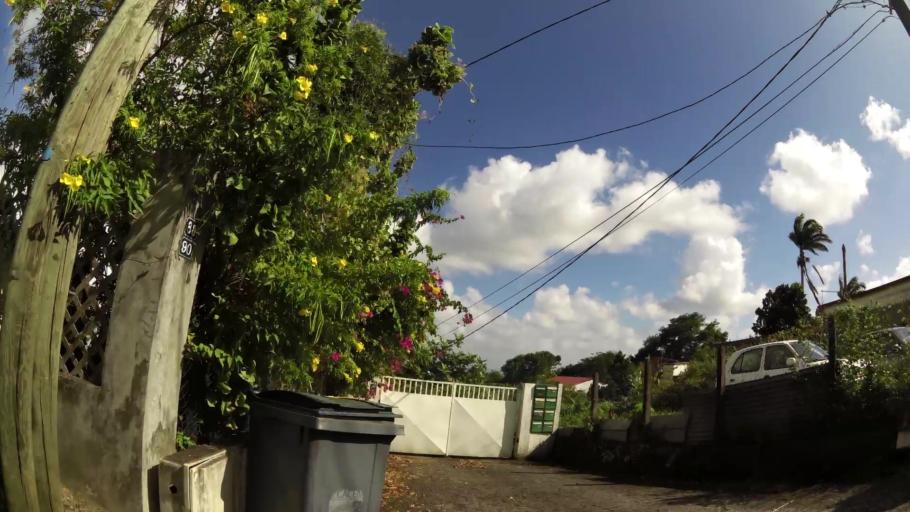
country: MQ
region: Martinique
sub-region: Martinique
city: Fort-de-France
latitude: 14.6270
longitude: -61.0492
